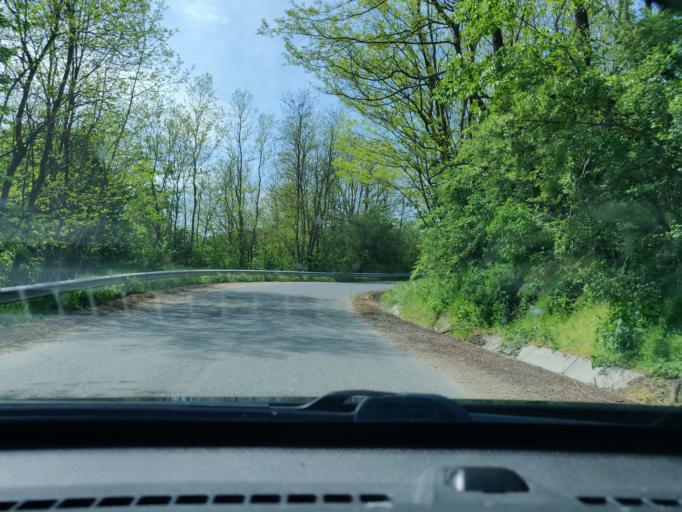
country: RO
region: Vrancea
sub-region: Comuna Vidra
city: Vidra
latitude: 45.9366
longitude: 26.8798
